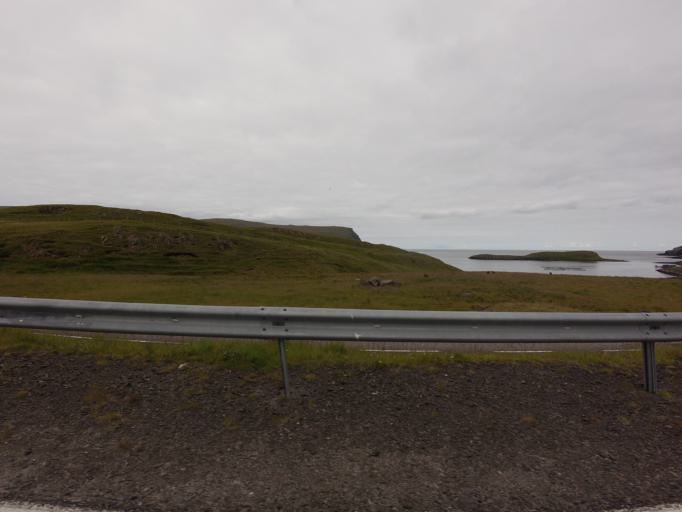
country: FO
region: Suduroy
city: Tvoroyri
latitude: 61.5305
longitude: -6.7970
